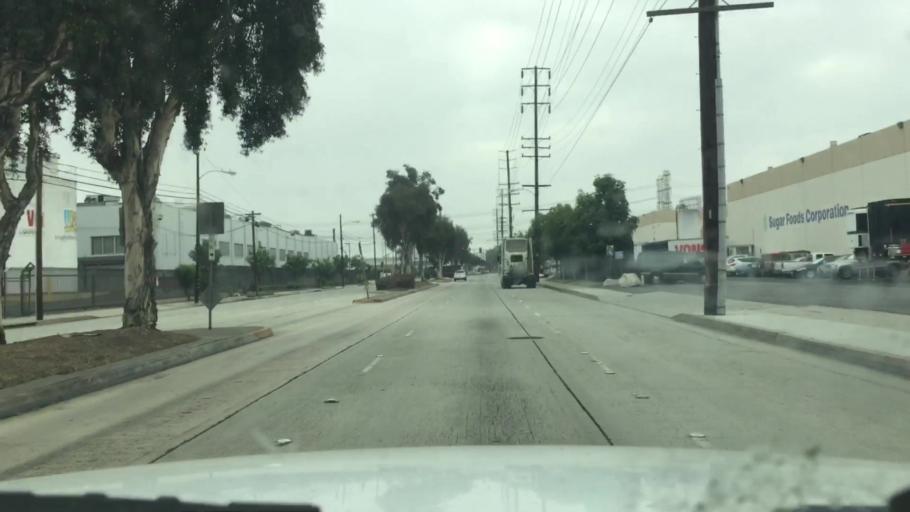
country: US
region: California
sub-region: Los Angeles County
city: Commerce
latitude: 33.9849
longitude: -118.1533
